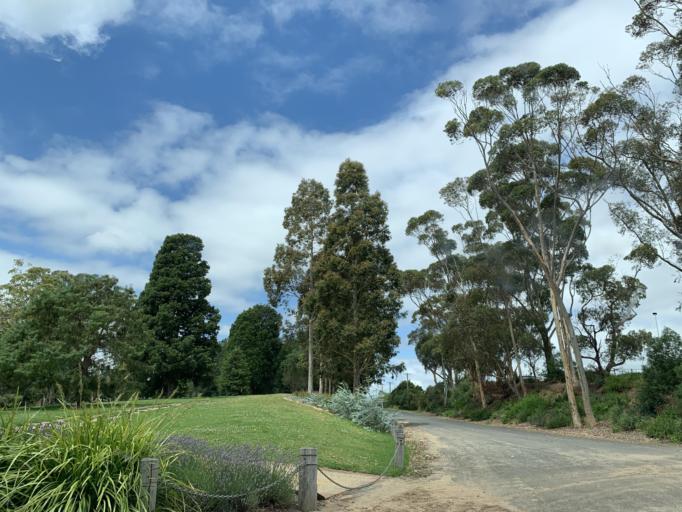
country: AU
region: Victoria
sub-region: Wellington
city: Sale
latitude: -38.1150
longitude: 147.0770
